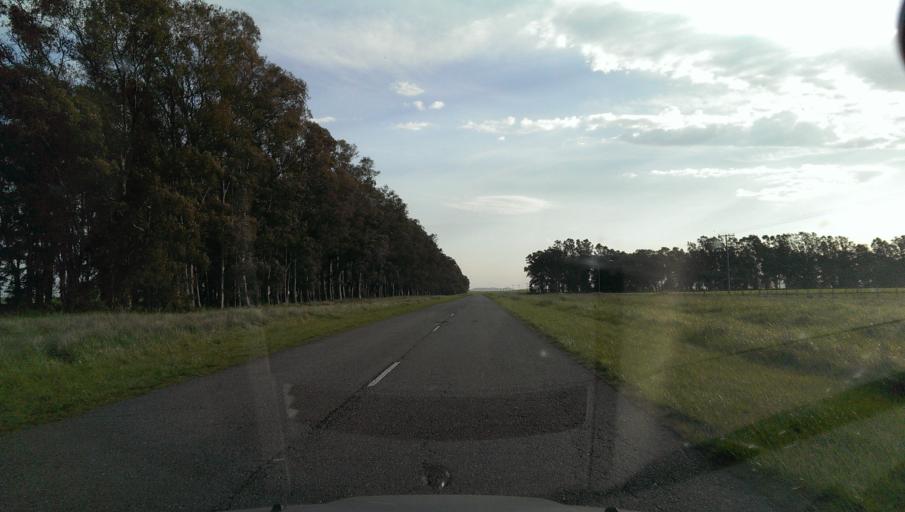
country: AR
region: Buenos Aires
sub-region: Partido de Coronel Suarez
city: Coronel Suarez
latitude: -37.8254
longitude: -61.8150
